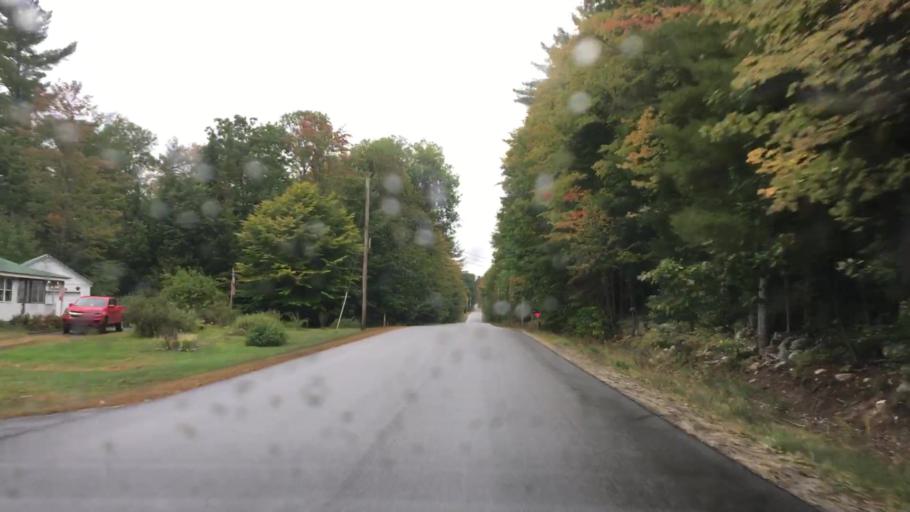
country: US
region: Maine
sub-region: Cumberland County
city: Harrison
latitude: 44.0826
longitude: -70.6457
